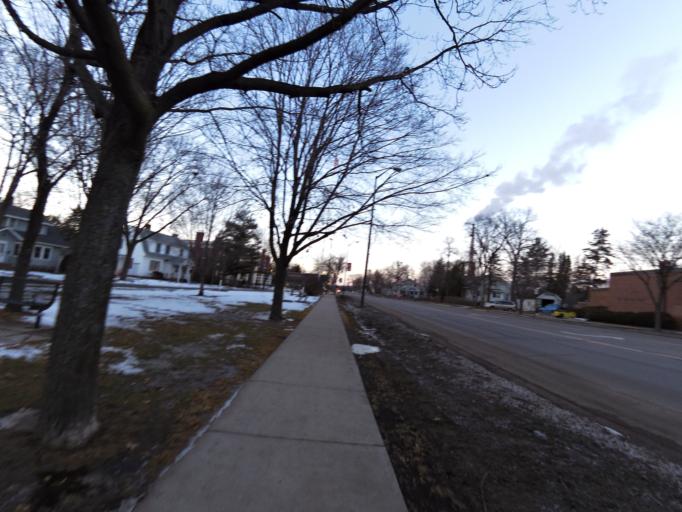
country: US
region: Minnesota
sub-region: Washington County
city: Bayport
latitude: 45.0207
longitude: -92.7807
